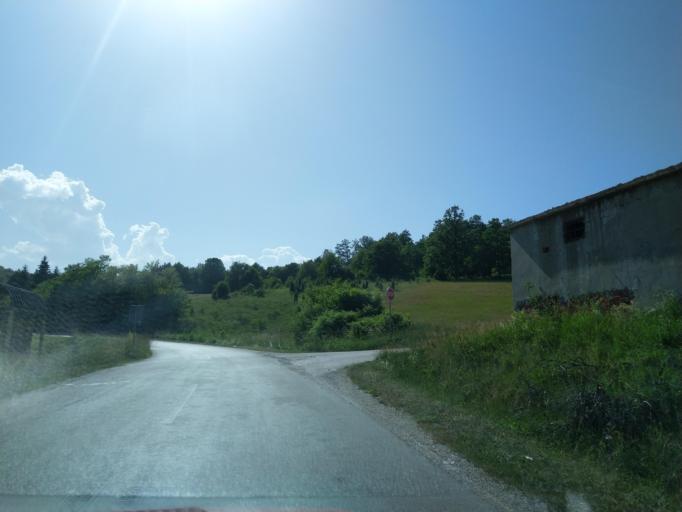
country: RS
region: Central Serbia
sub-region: Zlatiborski Okrug
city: Uzice
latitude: 43.8804
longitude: 19.7462
